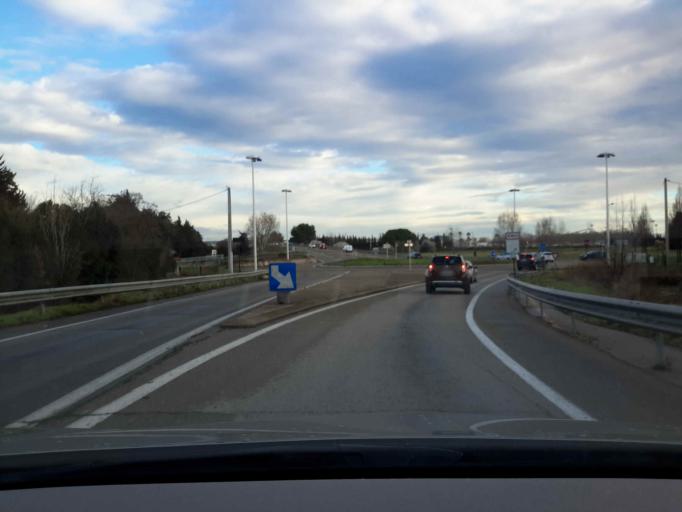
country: FR
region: Languedoc-Roussillon
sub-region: Departement du Gard
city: Nimes
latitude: 43.8092
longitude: 4.3544
